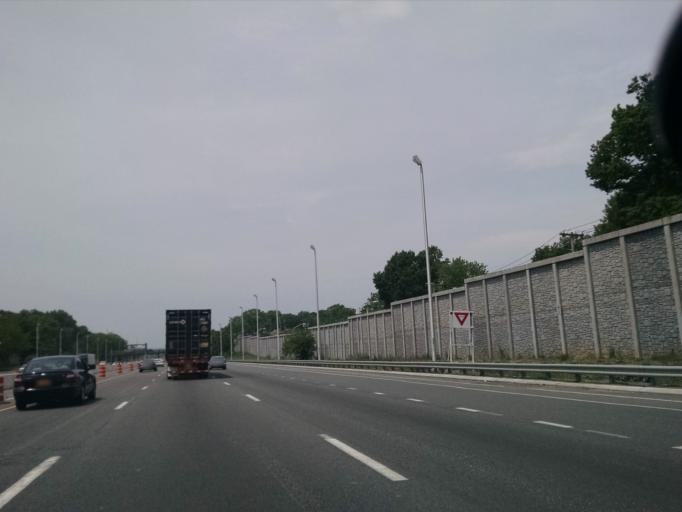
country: US
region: New York
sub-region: Richmond County
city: Bloomfield
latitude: 40.6081
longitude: -74.1361
